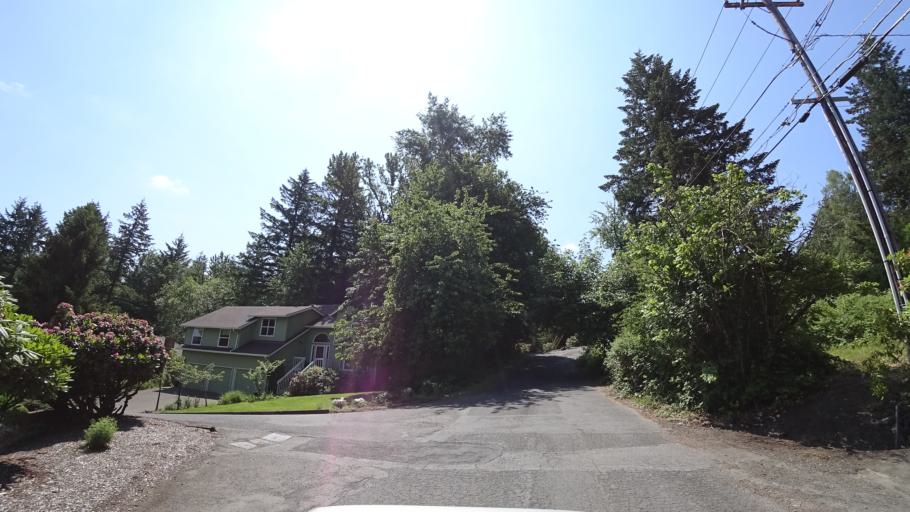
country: US
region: Oregon
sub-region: Clackamas County
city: Lake Oswego
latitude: 45.4390
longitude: -122.7115
